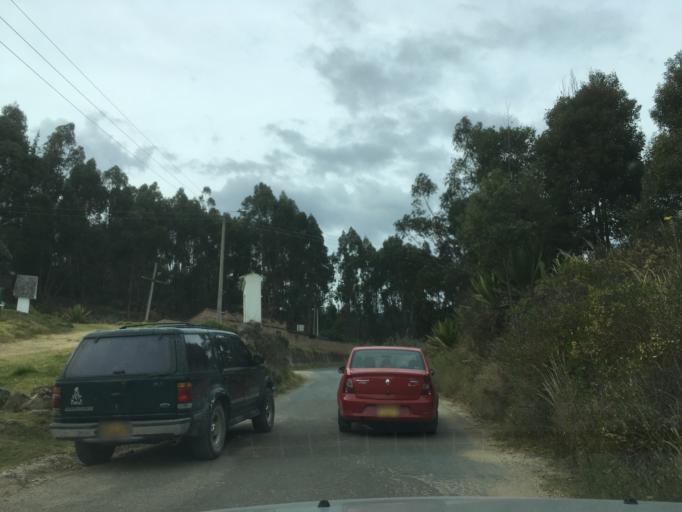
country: CO
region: Boyaca
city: Firavitoba
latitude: 5.6767
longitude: -73.0044
